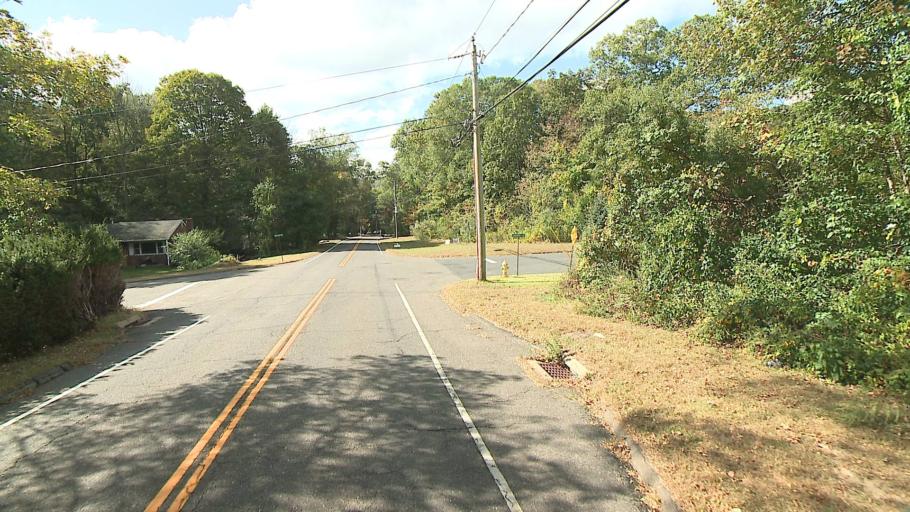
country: US
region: Connecticut
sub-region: New Haven County
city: Naugatuck
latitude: 41.4474
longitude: -73.0340
